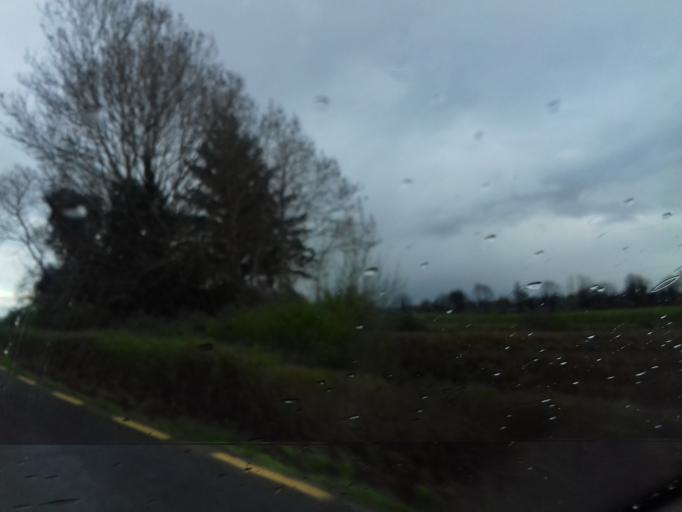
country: IE
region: Ulster
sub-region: An Cabhan
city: Ballyconnell
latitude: 54.1526
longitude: -7.7149
